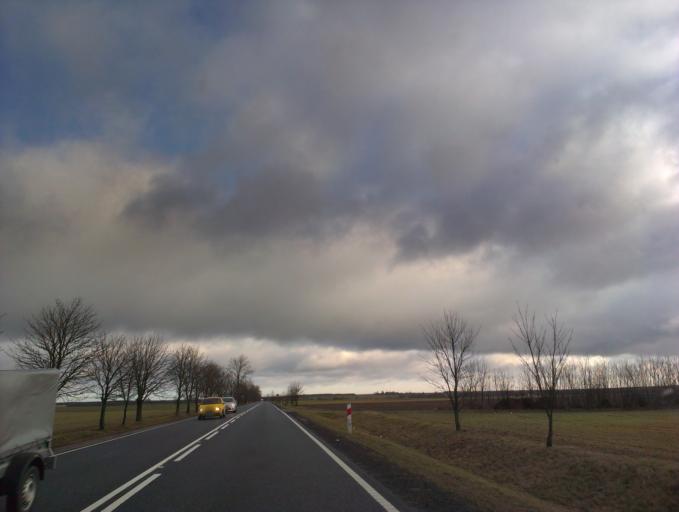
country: PL
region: Pomeranian Voivodeship
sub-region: Powiat czluchowski
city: Debrzno
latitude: 53.6210
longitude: 17.2076
